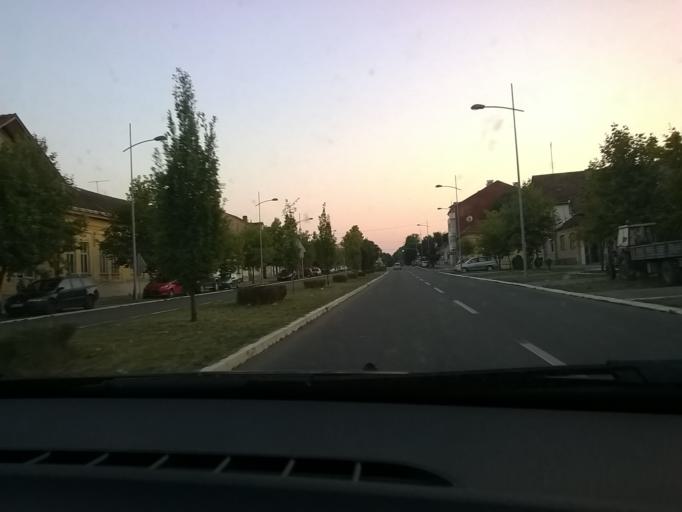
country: RS
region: Autonomna Pokrajina Vojvodina
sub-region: Juznobanatski Okrug
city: Vrsac
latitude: 45.1130
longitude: 21.2994
